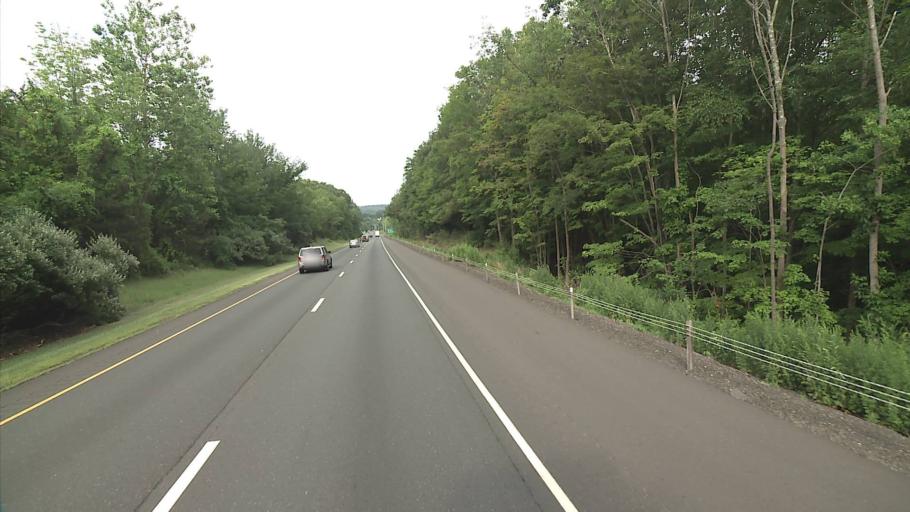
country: US
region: Connecticut
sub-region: New Haven County
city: Southbury
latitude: 41.4799
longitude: -73.2027
